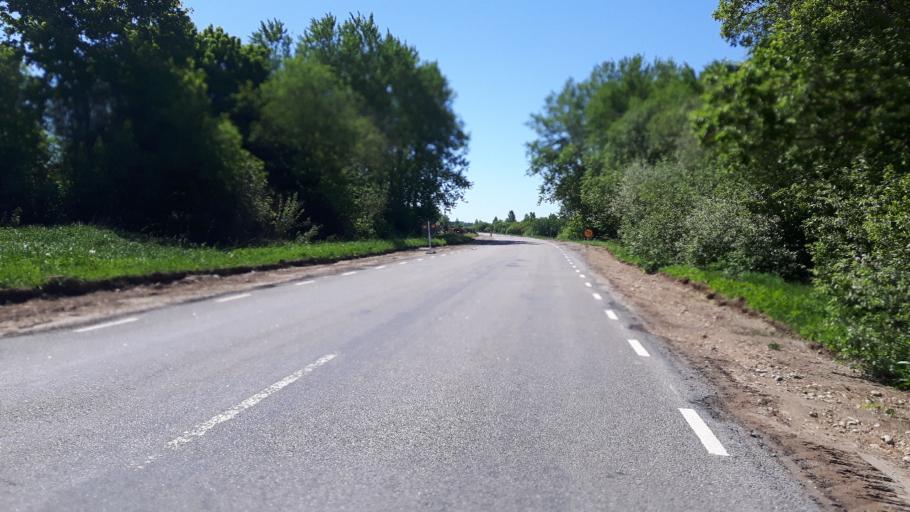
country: EE
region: Ida-Virumaa
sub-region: Narva-Joesuu linn
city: Narva-Joesuu
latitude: 59.3924
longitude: 27.9231
